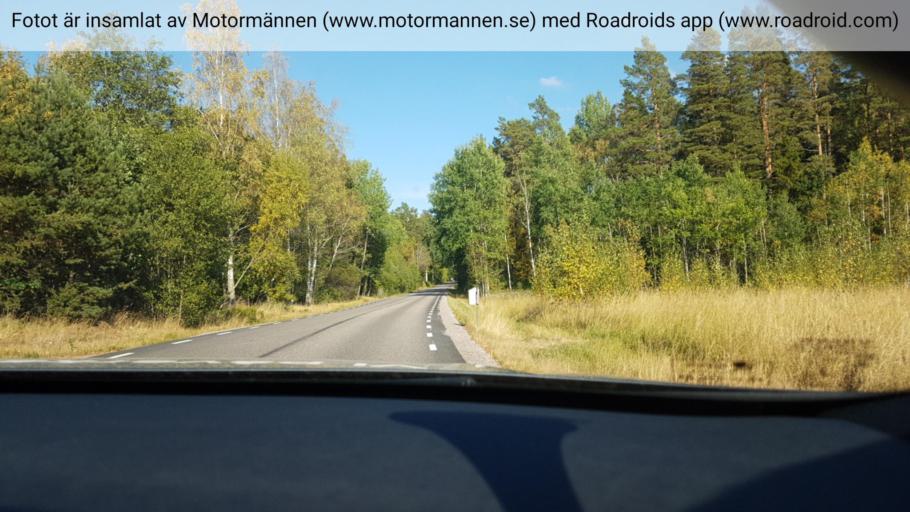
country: SE
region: Vaestra Goetaland
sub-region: Gotene Kommun
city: Goetene
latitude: 58.6364
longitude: 13.5497
